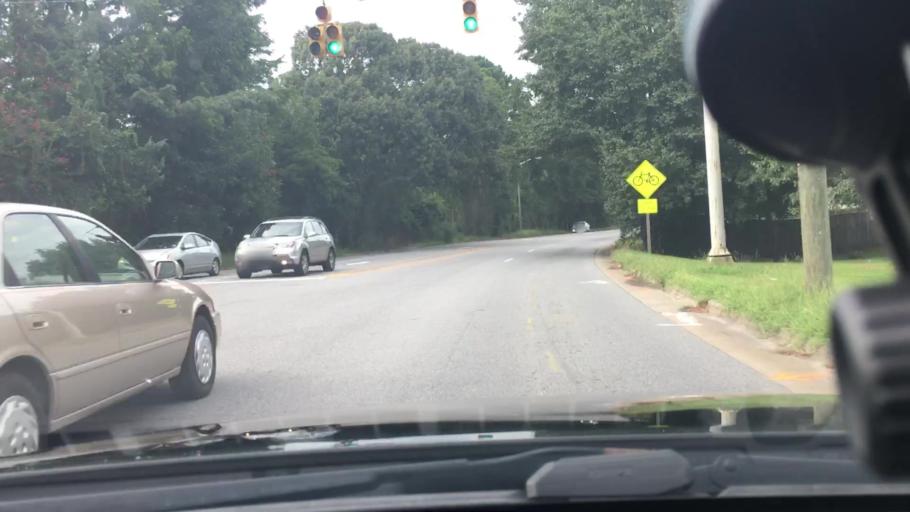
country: US
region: North Carolina
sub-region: Pitt County
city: Greenville
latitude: 35.5866
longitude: -77.3469
